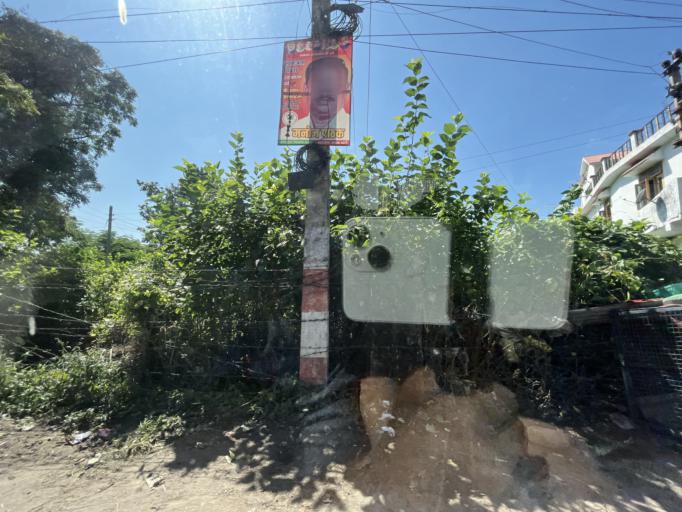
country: IN
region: Uttarakhand
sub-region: Naini Tal
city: Haldwani
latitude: 29.2102
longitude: 79.4645
